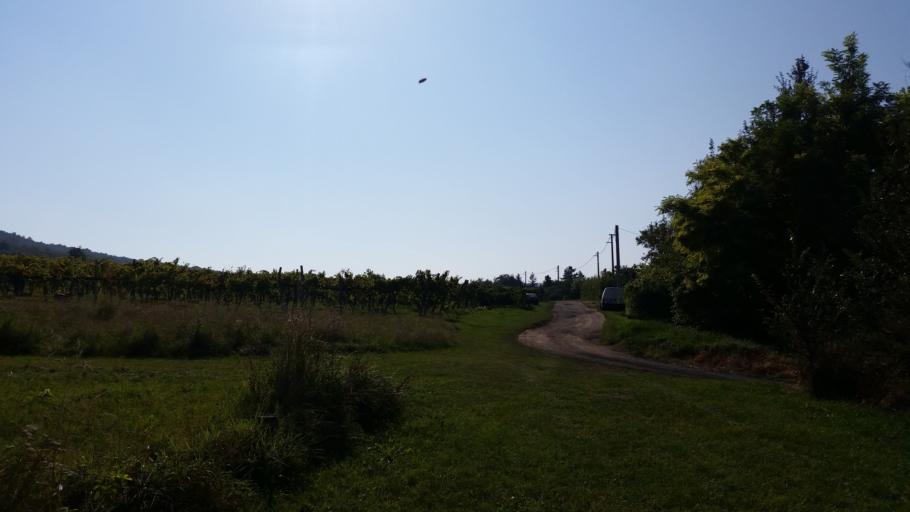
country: HU
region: Pest
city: Telki
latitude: 47.5498
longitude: 18.8320
